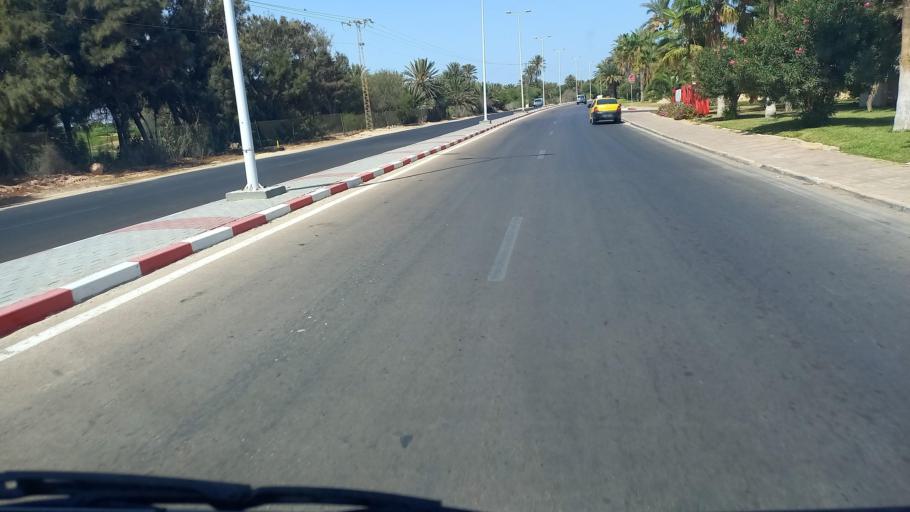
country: TN
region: Madanin
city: Midoun
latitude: 33.8253
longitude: 11.0208
